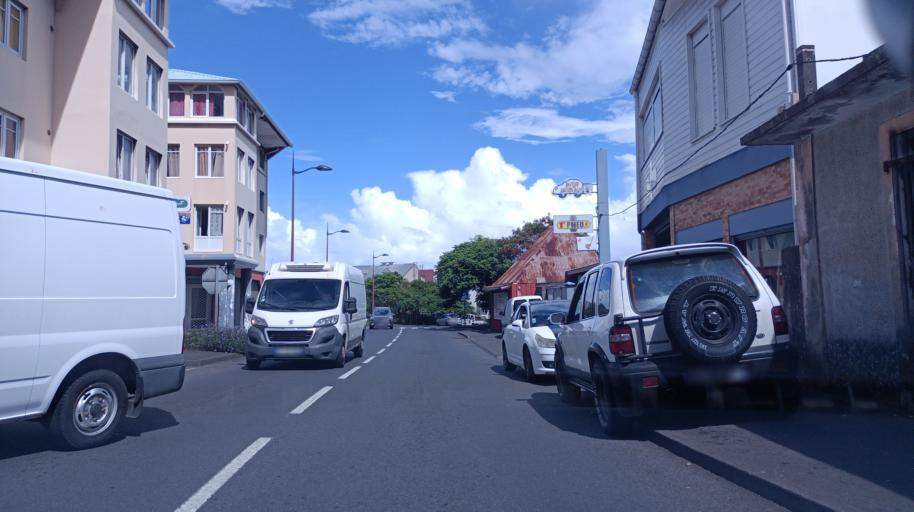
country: RE
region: Reunion
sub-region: Reunion
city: Saint-Joseph
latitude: -21.3804
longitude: 55.6152
